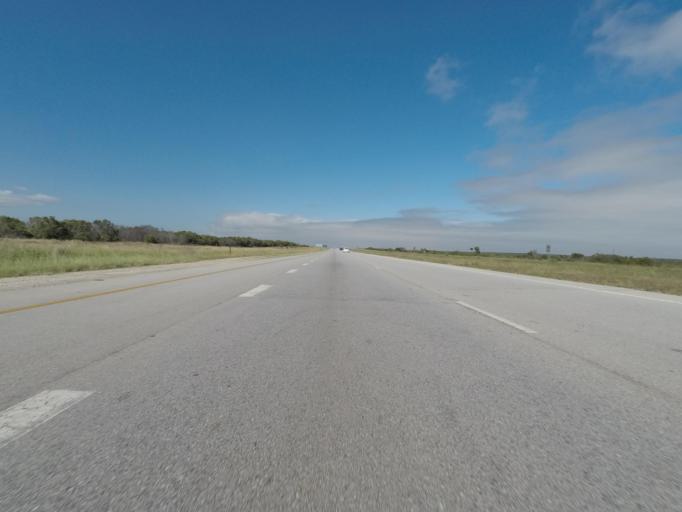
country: ZA
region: Eastern Cape
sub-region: Nelson Mandela Bay Metropolitan Municipality
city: Port Elizabeth
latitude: -33.7552
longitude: 25.7028
